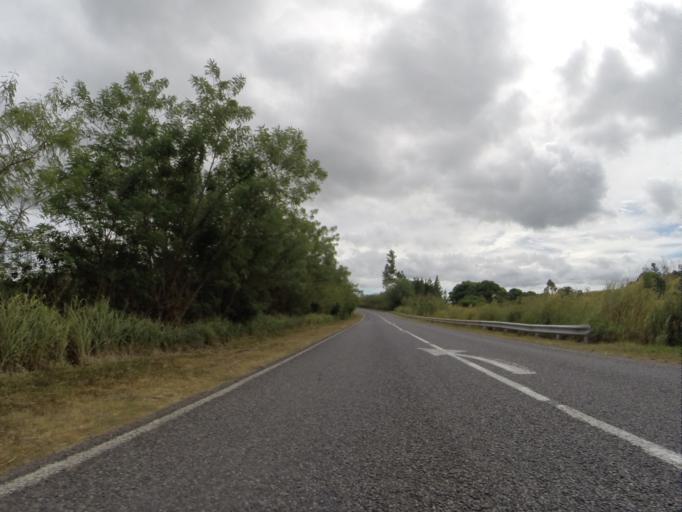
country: FJ
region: Western
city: Nadi
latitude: -18.0262
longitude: 177.3314
